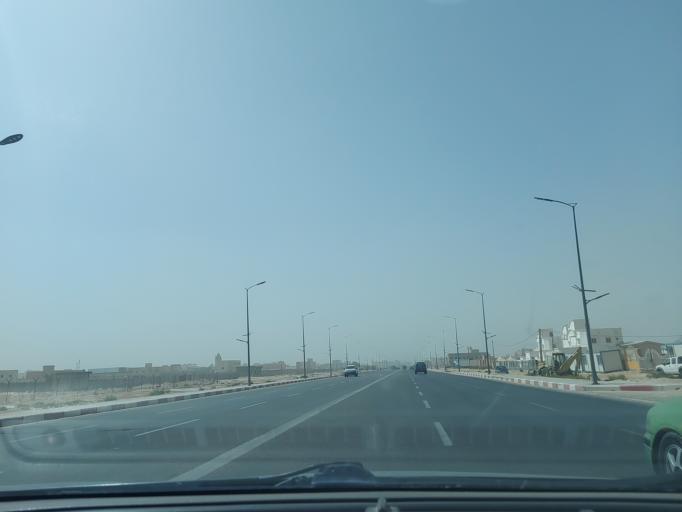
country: MR
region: Nouakchott
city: Nouakchott
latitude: 18.1340
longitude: -16.0045
